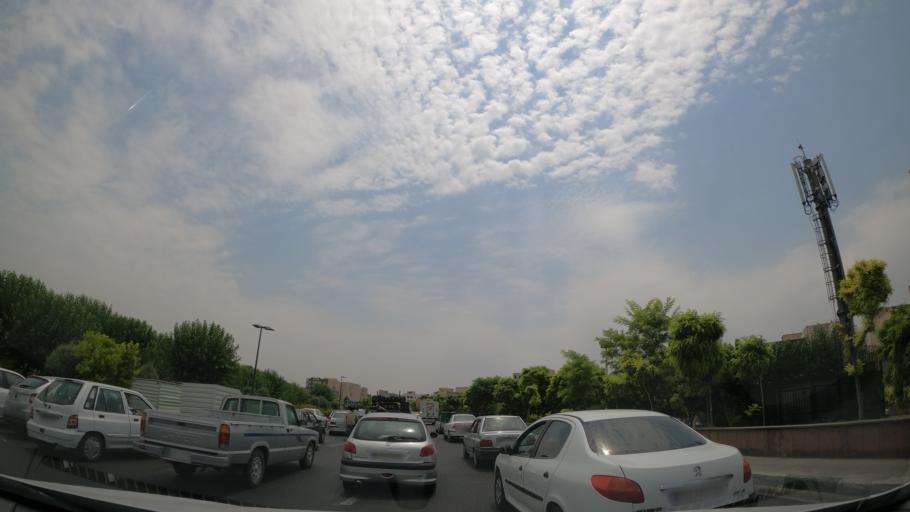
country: IR
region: Tehran
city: Tehran
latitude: 35.6788
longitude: 51.3384
